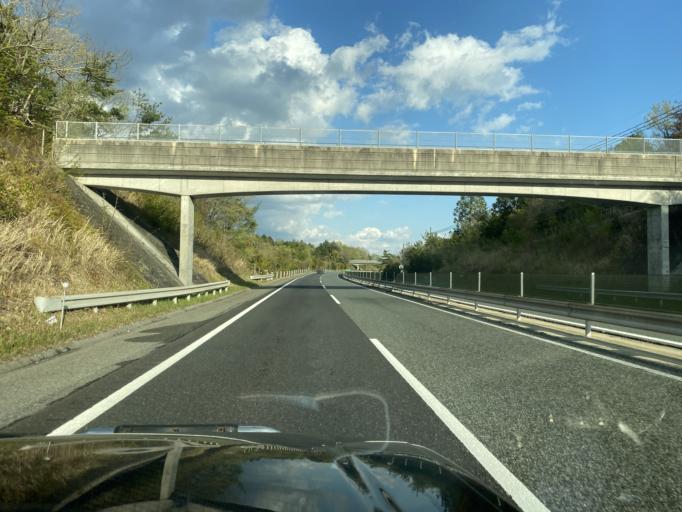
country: JP
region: Hyogo
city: Sandacho
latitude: 34.9427
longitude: 135.1522
